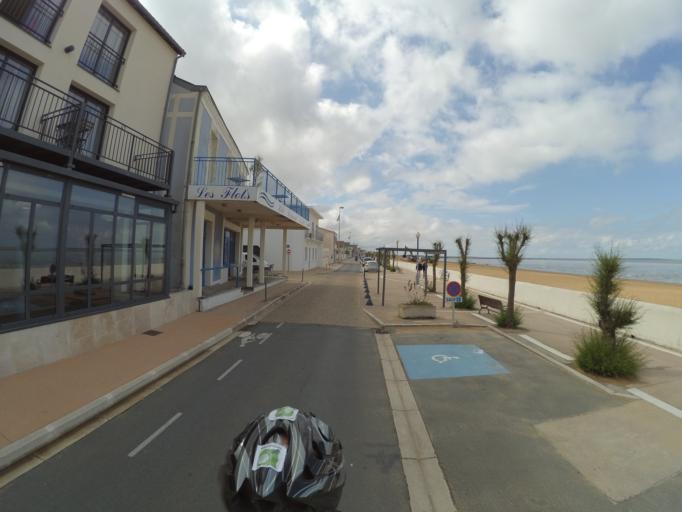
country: FR
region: Poitou-Charentes
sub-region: Departement de la Charente-Maritime
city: Chatelaillon-Plage
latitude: 46.0749
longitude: -1.0936
